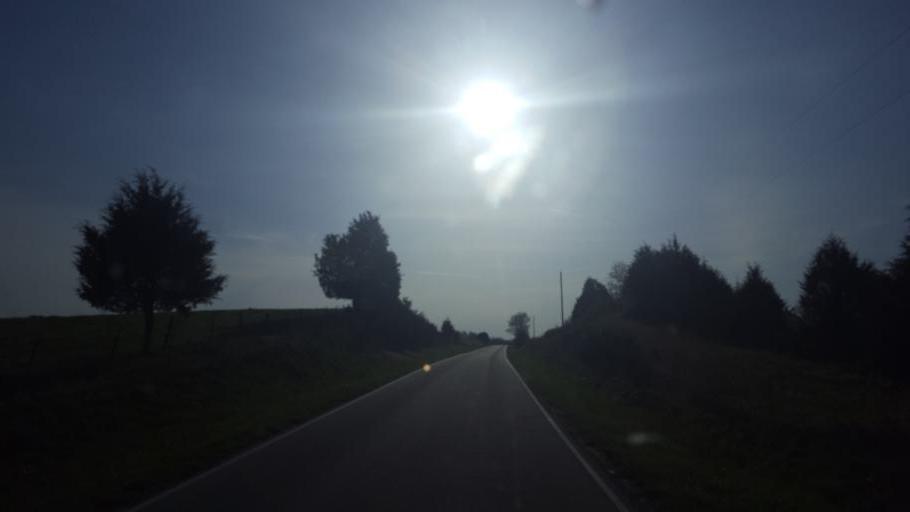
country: US
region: Kentucky
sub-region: Hart County
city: Munfordville
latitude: 37.4857
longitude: -85.9433
